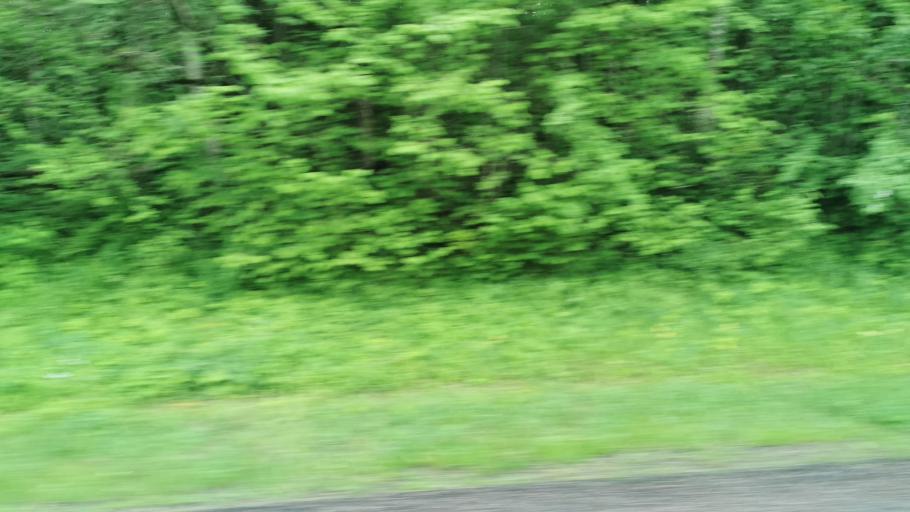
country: EE
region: Laeaene-Virumaa
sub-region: Rakvere linn
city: Rakvere
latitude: 59.2710
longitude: 26.3541
